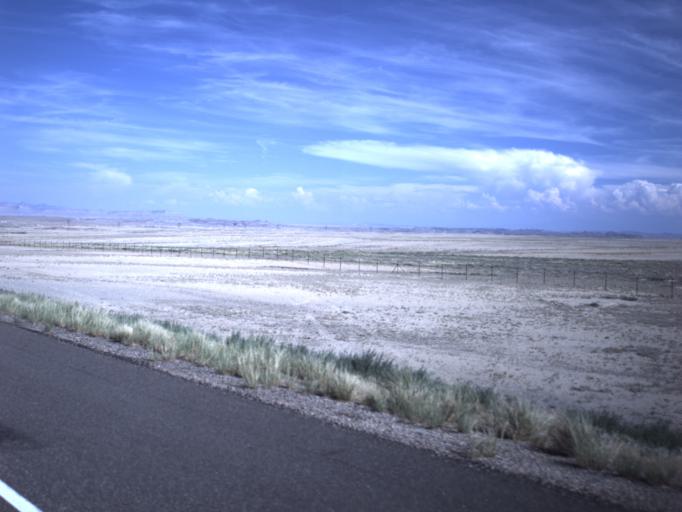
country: US
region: Utah
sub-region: Carbon County
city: East Carbon City
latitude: 38.9568
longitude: -110.2994
